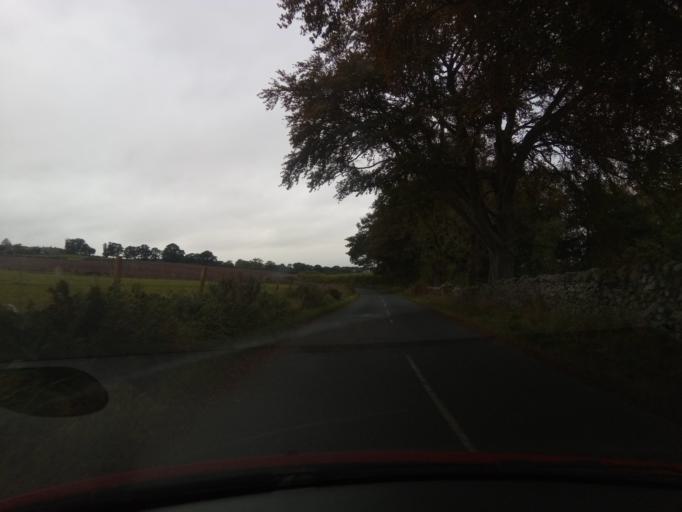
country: GB
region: Scotland
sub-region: The Scottish Borders
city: Saint Boswells
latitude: 55.5149
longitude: -2.6123
